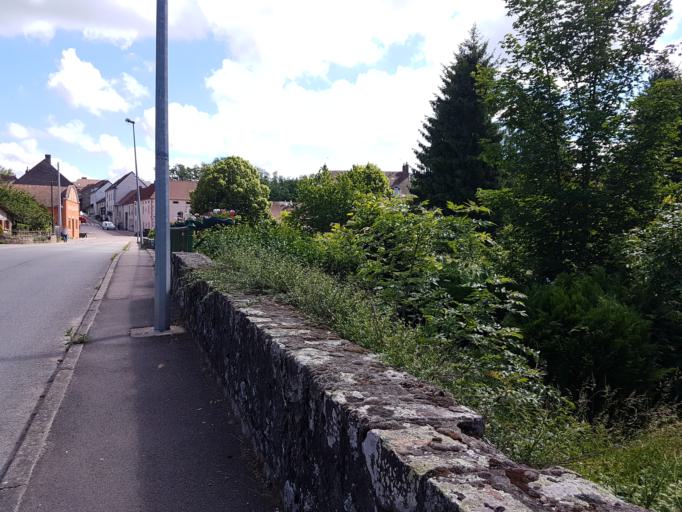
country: FR
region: Bourgogne
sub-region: Departement de Saone-et-Loire
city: Epinac
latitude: 46.9883
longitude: 4.5102
